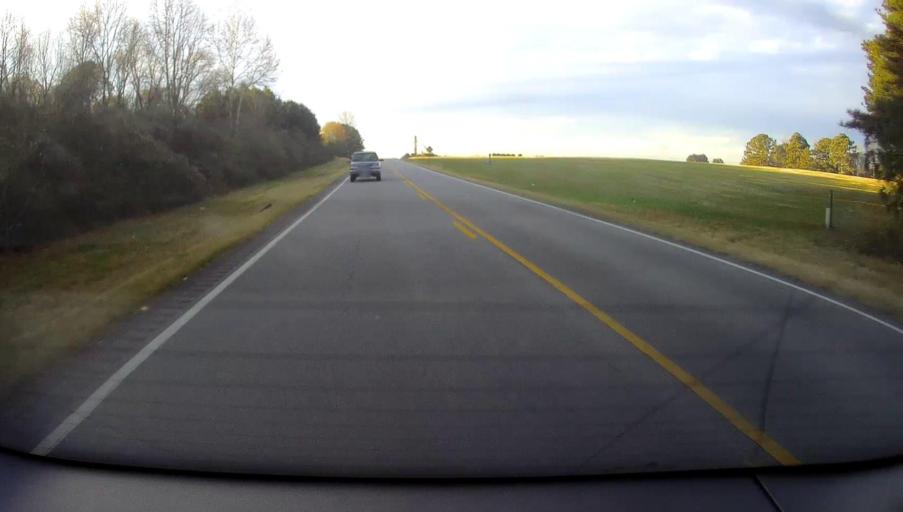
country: US
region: Alabama
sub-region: Blount County
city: Oneonta
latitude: 34.1018
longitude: -86.3675
